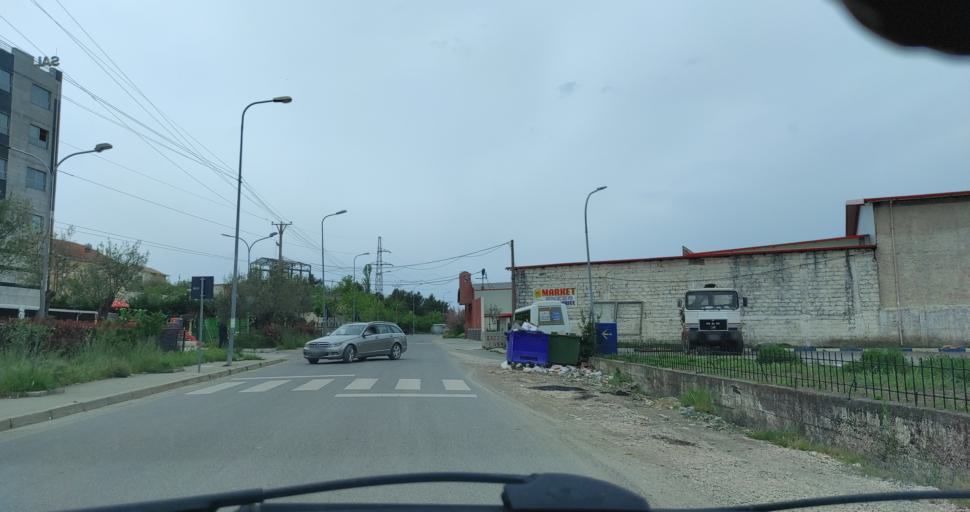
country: AL
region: Lezhe
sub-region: Rrethi i Kurbinit
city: Lac
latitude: 41.6215
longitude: 19.7092
